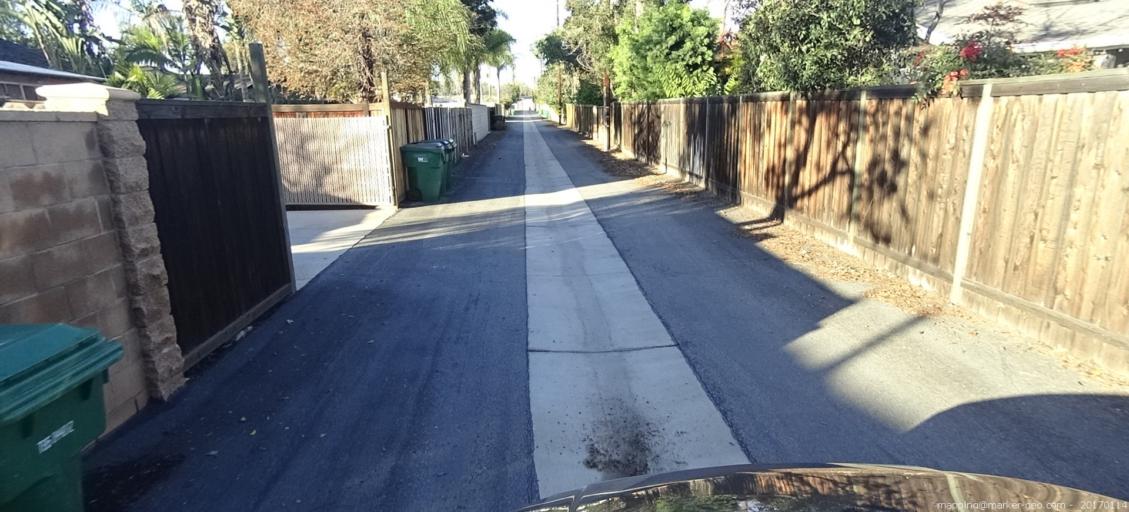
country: US
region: California
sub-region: Orange County
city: Tustin
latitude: 33.7674
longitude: -117.8196
